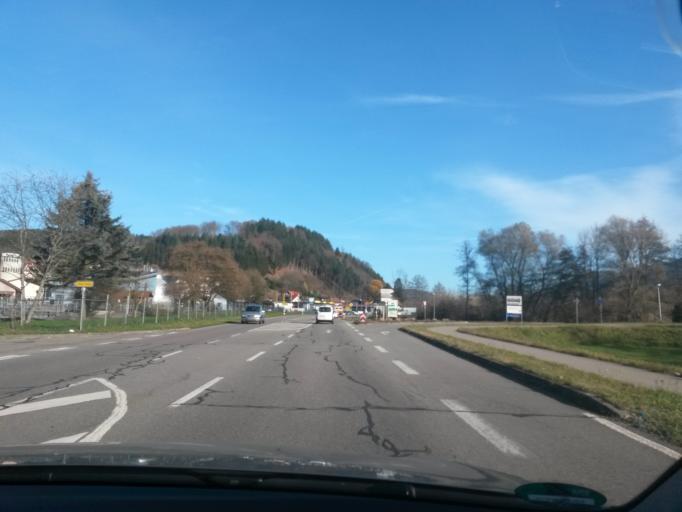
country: DE
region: Baden-Wuerttemberg
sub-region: Freiburg Region
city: Elzach
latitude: 48.1657
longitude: 8.0581
